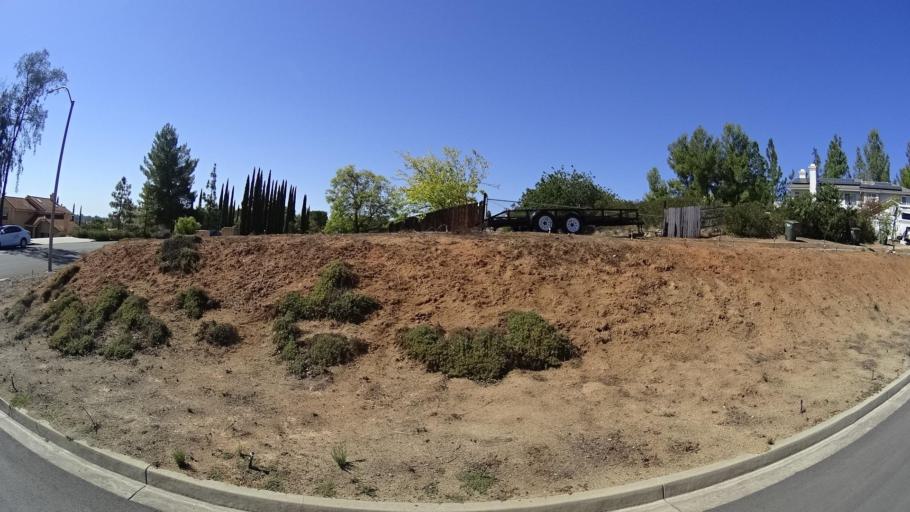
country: US
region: California
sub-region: San Diego County
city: Alpine
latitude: 32.8401
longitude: -116.7638
